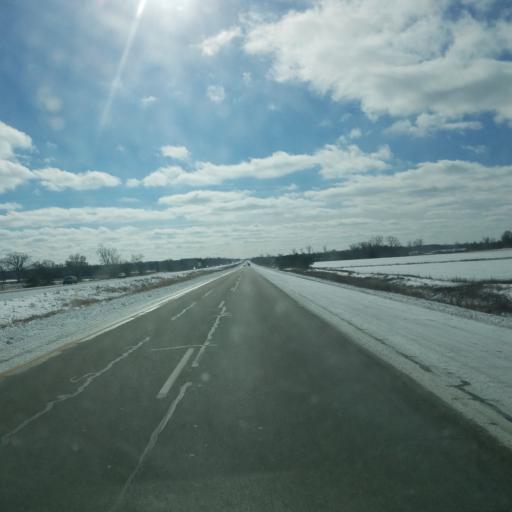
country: US
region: Michigan
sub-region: Clinton County
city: Saint Johns
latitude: 42.9822
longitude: -84.5190
